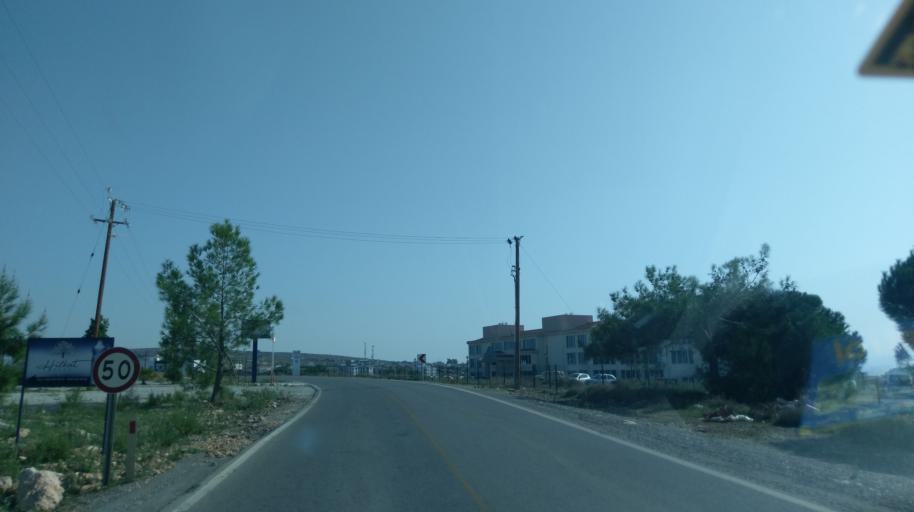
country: CY
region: Lefkosia
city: Morfou
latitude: 35.2511
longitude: 33.0331
